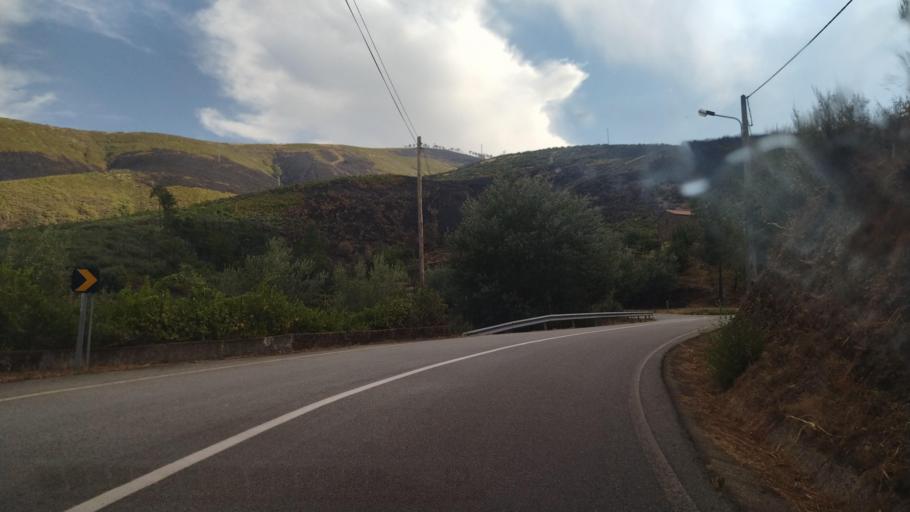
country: PT
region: Castelo Branco
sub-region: Covilha
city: Teixoso
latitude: 40.3726
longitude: -7.4563
